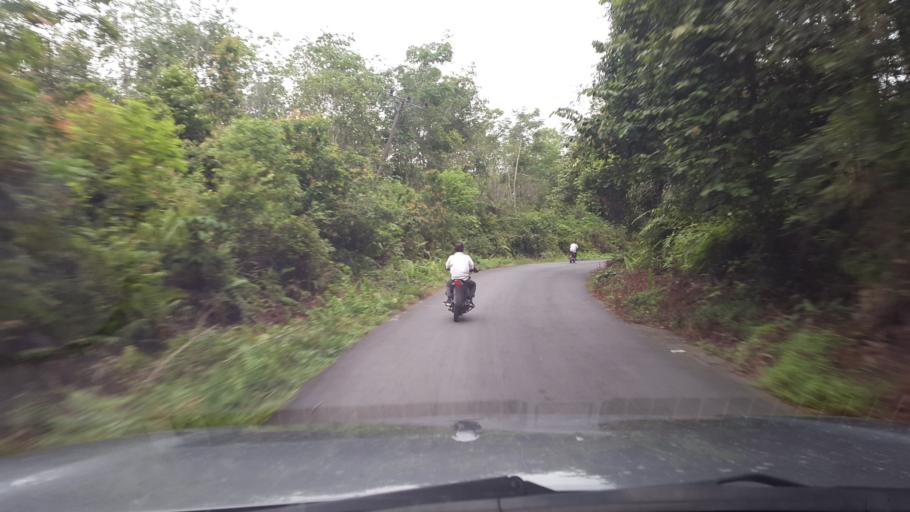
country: ID
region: South Sumatra
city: Gunungmenang
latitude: -3.1687
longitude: 104.0062
